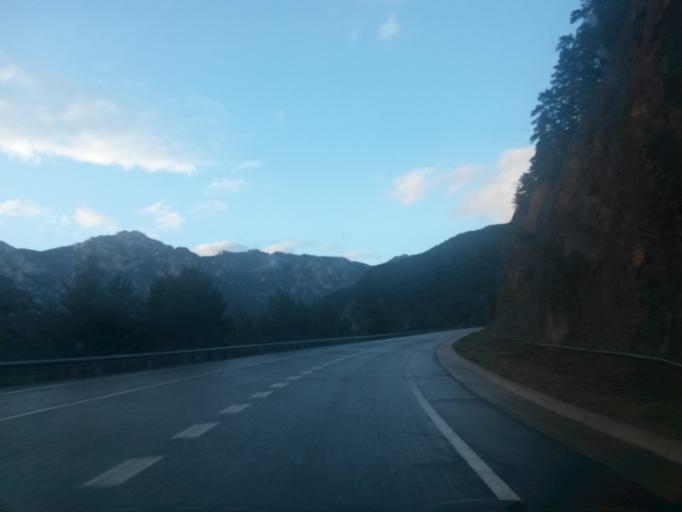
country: ES
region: Catalonia
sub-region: Provincia de Barcelona
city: Baga
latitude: 42.2662
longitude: 1.8522
